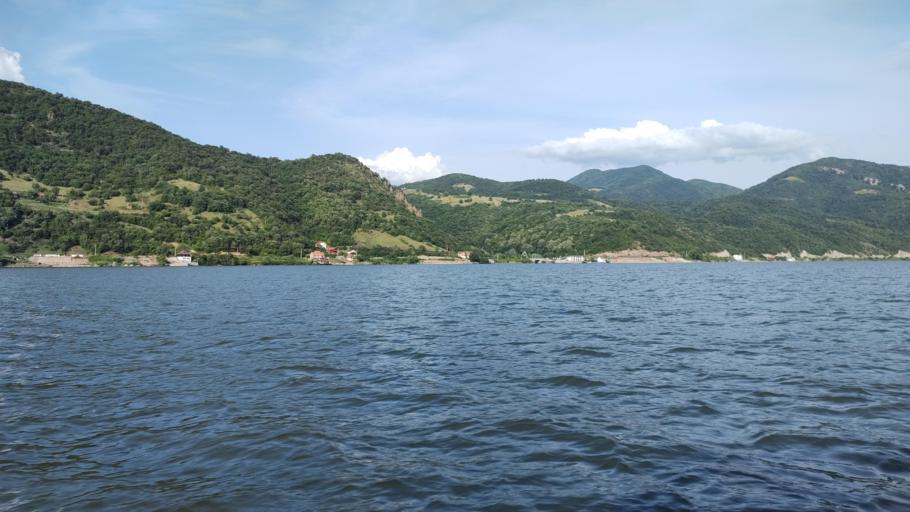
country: RO
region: Mehedinti
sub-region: Comuna Svinita
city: Svinita
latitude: 44.5397
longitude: 22.0533
